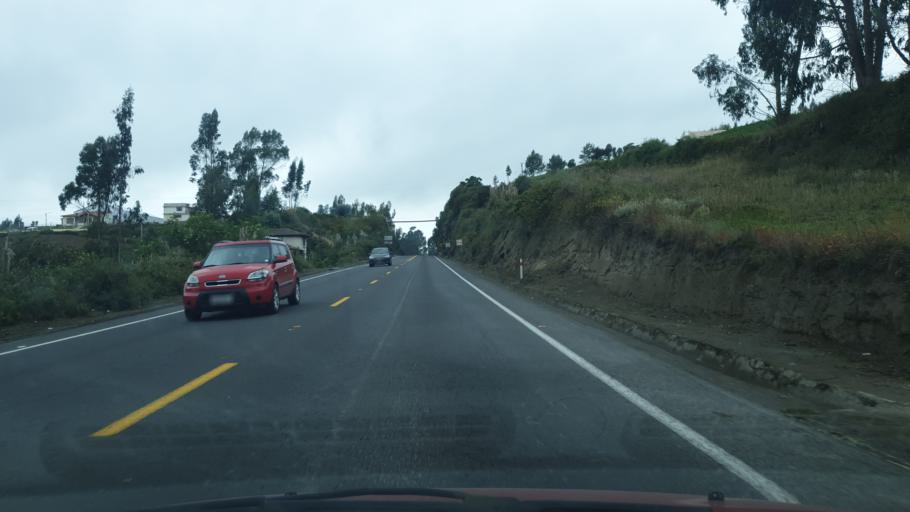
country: EC
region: Tungurahua
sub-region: Canton Quero
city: Quero
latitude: -1.3743
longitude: -78.6510
